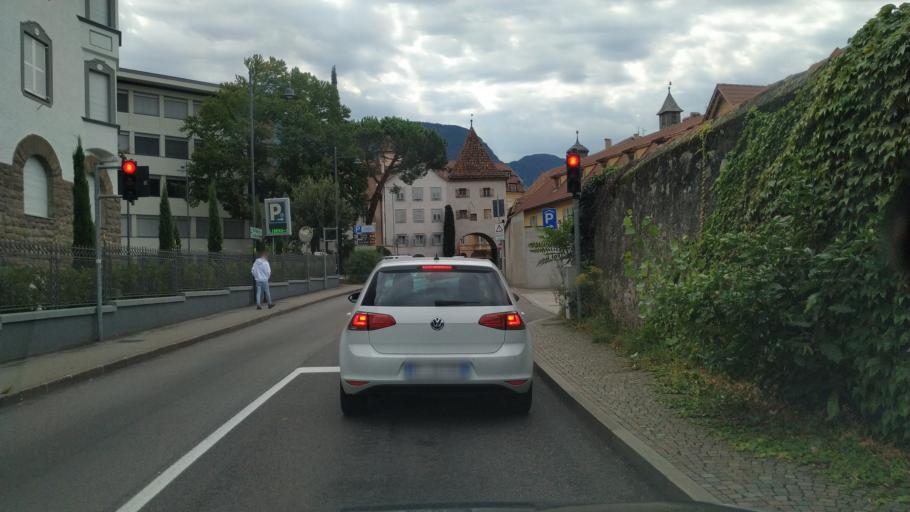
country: IT
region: Trentino-Alto Adige
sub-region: Bolzano
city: Merano
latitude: 46.6744
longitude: 11.1586
